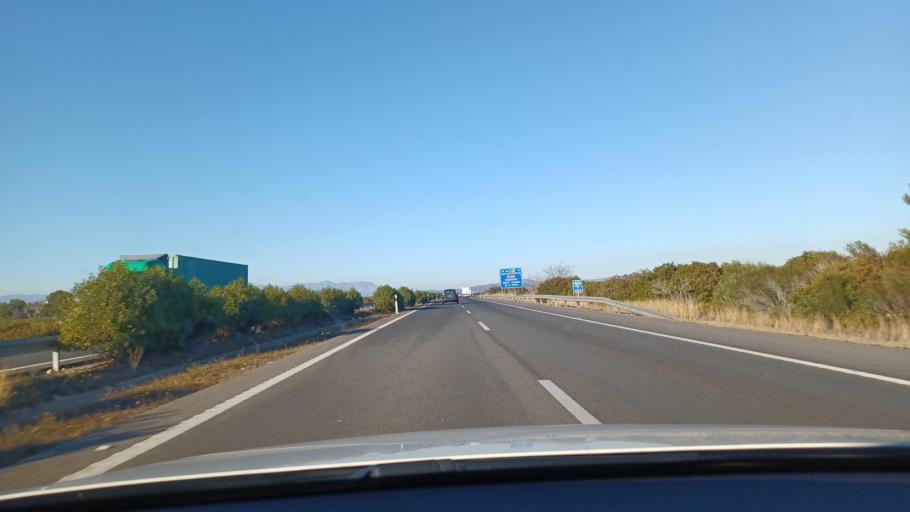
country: ES
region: Valencia
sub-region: Provincia de Castello
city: Vinaros
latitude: 40.5108
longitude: 0.4152
